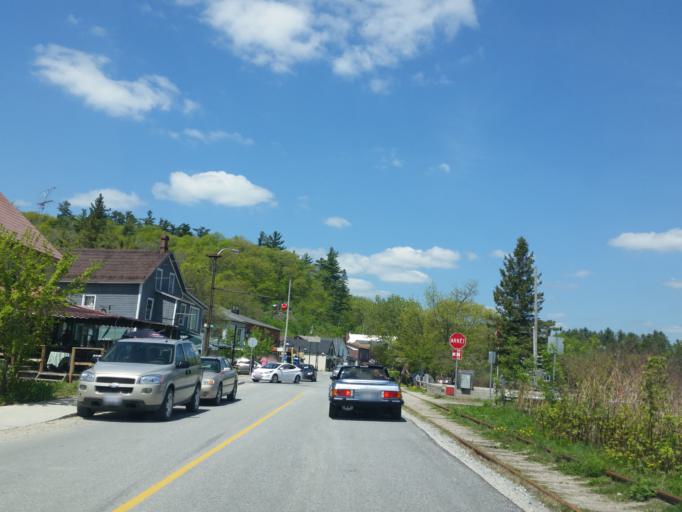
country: CA
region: Quebec
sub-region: Outaouais
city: Wakefield
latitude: 45.6329
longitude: -75.9273
